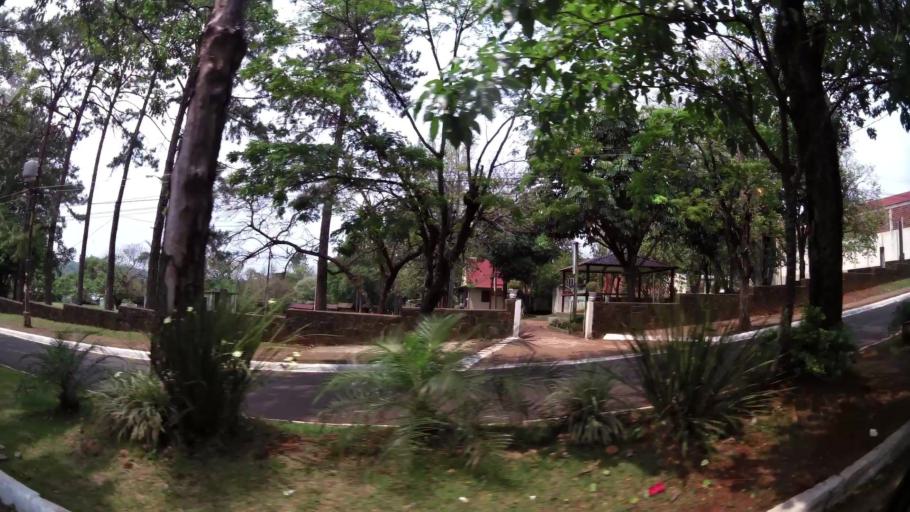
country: BR
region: Parana
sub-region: Foz Do Iguacu
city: Foz do Iguacu
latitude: -25.5580
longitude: -54.6033
